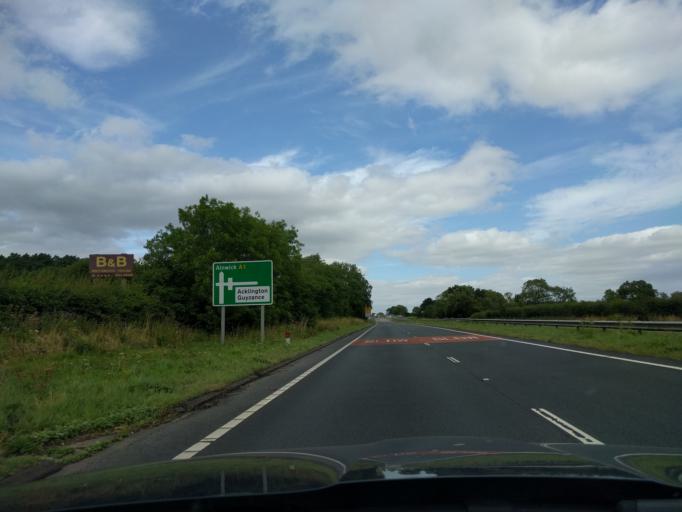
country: GB
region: England
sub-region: Northumberland
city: Felton
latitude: 55.3267
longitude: -1.7248
